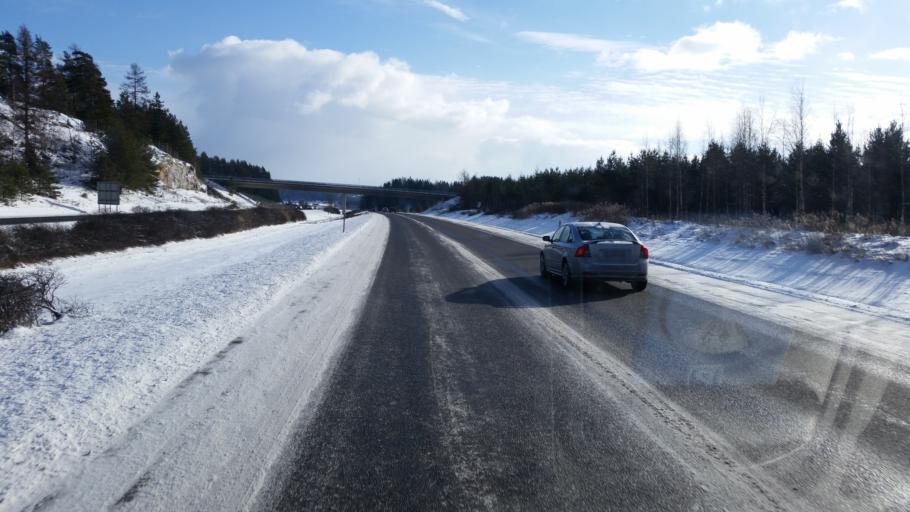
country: FI
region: Varsinais-Suomi
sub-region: Turku
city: Paimio
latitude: 60.4376
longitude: 22.6314
